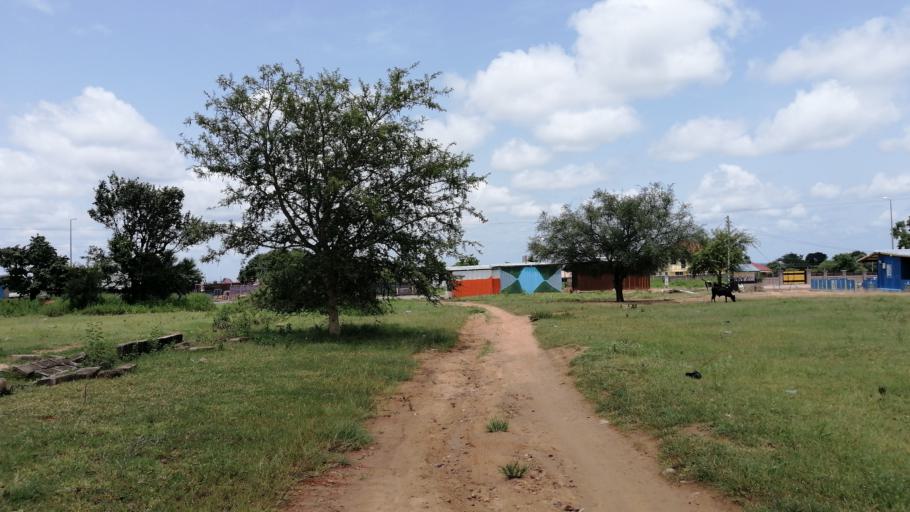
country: GH
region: Upper East
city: Bolgatanga
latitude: 10.8067
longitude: -0.8921
